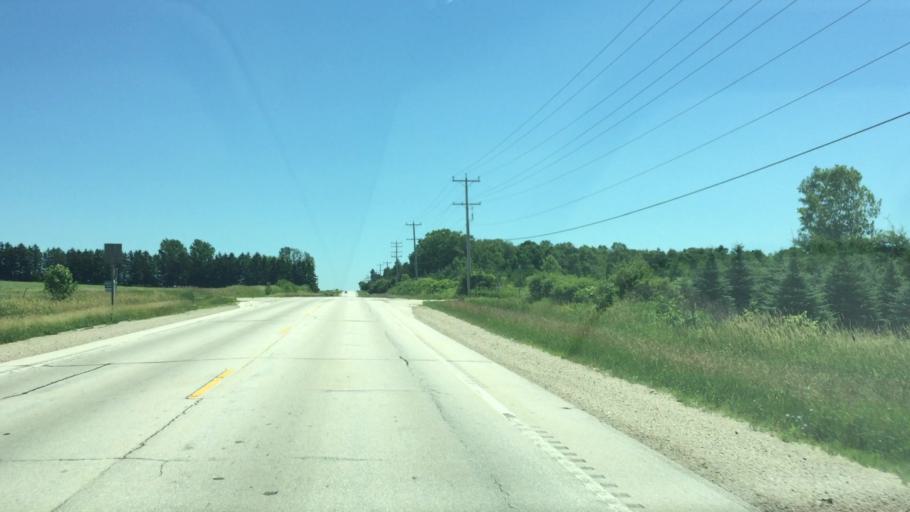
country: US
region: Wisconsin
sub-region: Calumet County
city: Sherwood
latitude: 44.1408
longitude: -88.2458
